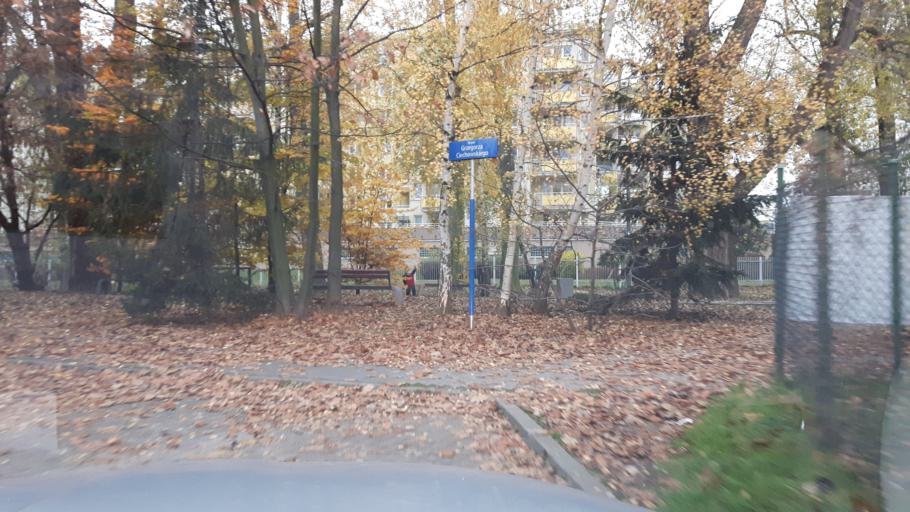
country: PL
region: Masovian Voivodeship
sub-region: Warszawa
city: Targowek
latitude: 52.2917
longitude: 21.0537
